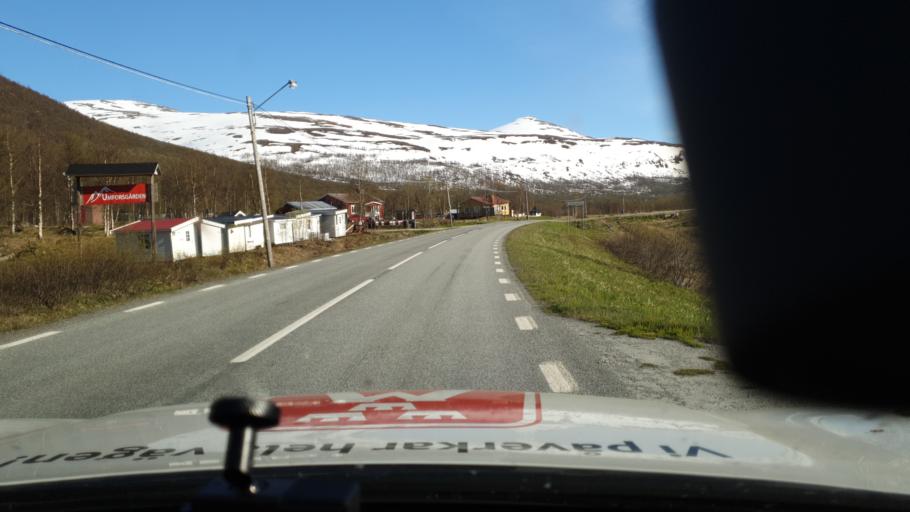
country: NO
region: Nordland
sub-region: Rana
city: Mo i Rana
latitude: 65.9522
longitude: 15.0381
